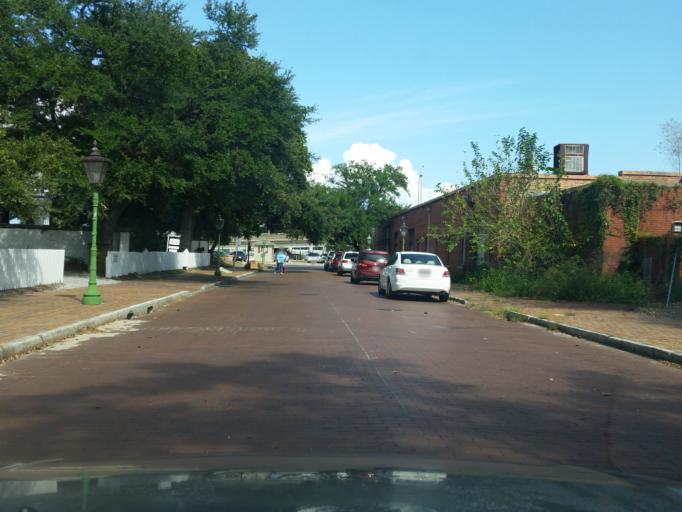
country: US
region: Alabama
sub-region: Mobile County
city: Mobile
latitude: 30.6882
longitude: -88.0405
